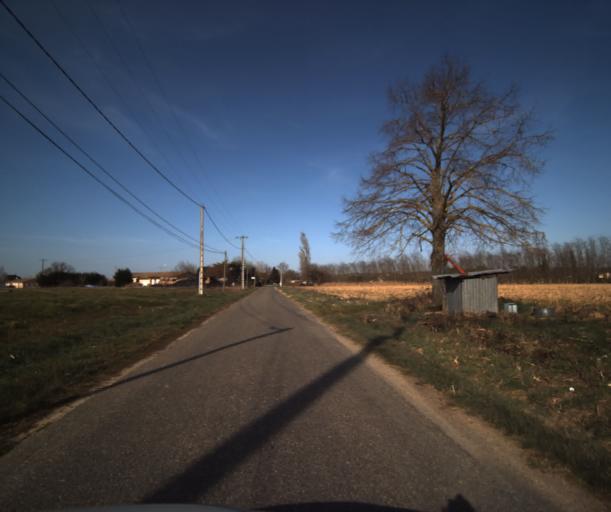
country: FR
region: Midi-Pyrenees
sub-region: Departement du Tarn-et-Garonne
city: Labastide-Saint-Pierre
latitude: 43.9263
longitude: 1.3540
